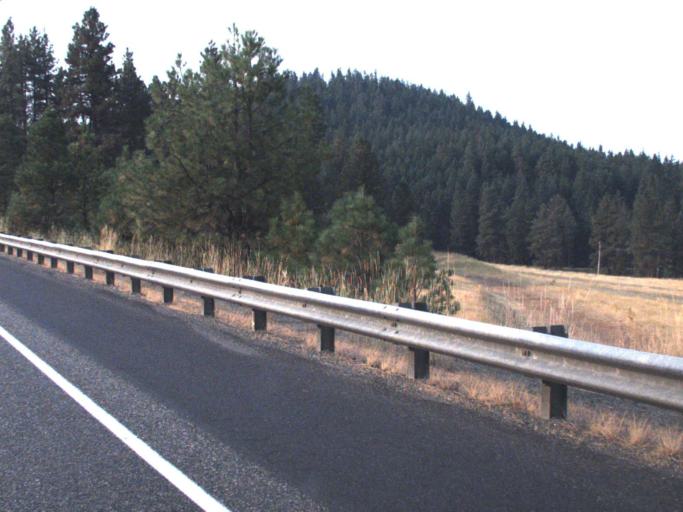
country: US
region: Washington
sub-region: Kittitas County
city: Cle Elum
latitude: 47.1952
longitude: -120.7067
